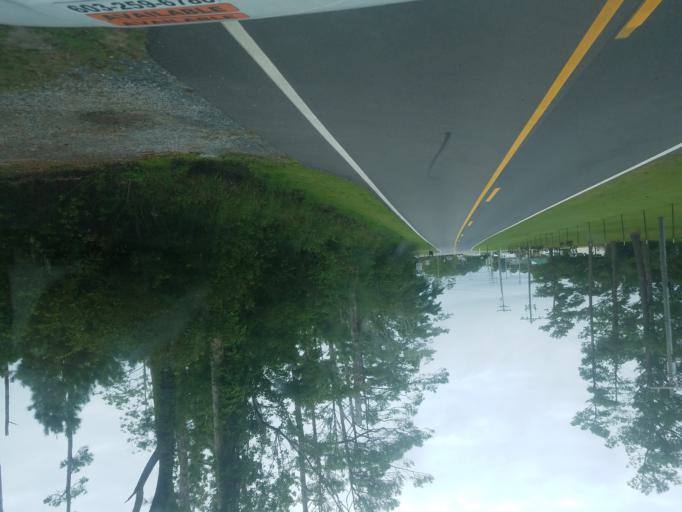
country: US
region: North Carolina
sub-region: Dare County
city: Manteo
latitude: 35.8840
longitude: -75.7615
